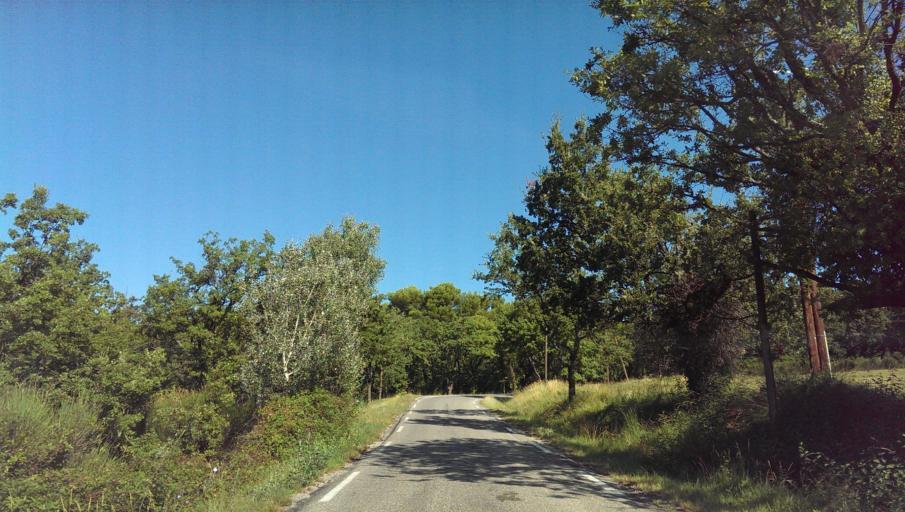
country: FR
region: Provence-Alpes-Cote d'Azur
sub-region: Departement du Vaucluse
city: Gordes
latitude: 43.9479
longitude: 5.2109
